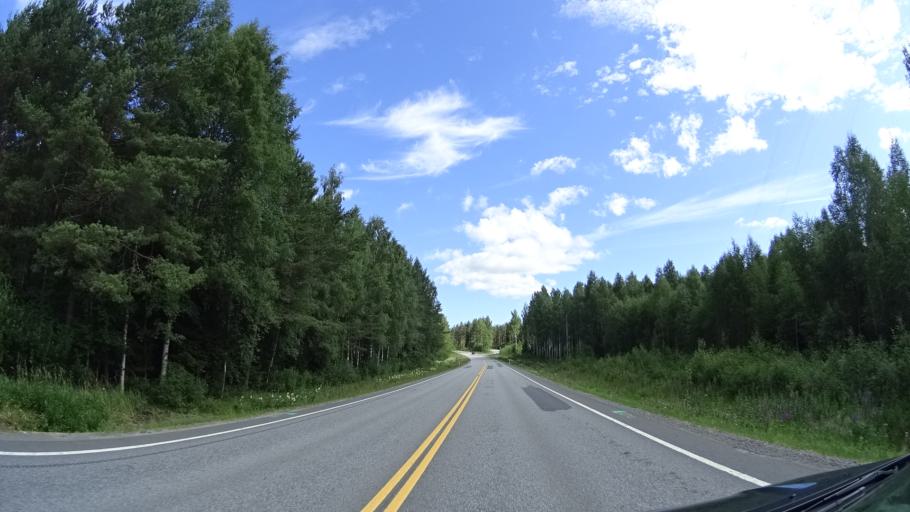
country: FI
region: Pirkanmaa
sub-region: Luoteis-Pirkanmaa
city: Kihnioe
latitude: 62.1518
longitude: 23.1599
